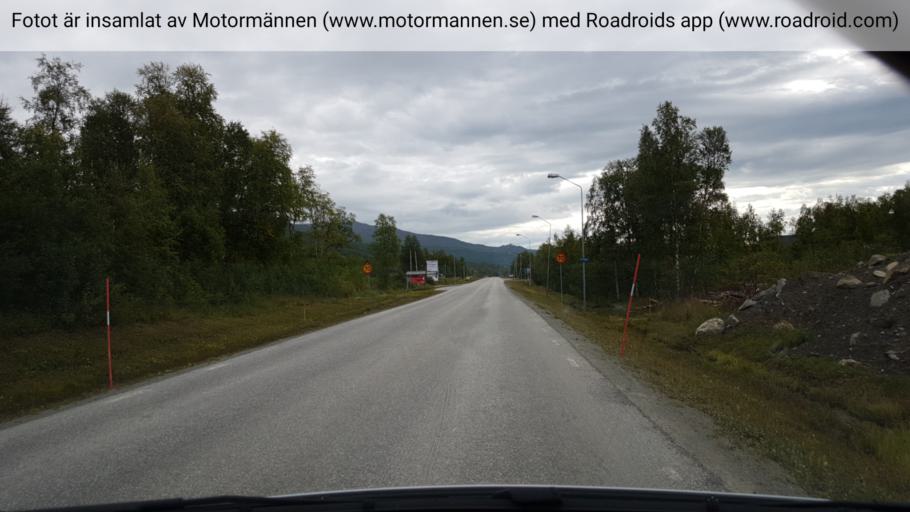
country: NO
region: Nordland
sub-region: Rana
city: Mo i Rana
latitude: 65.8299
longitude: 15.0645
